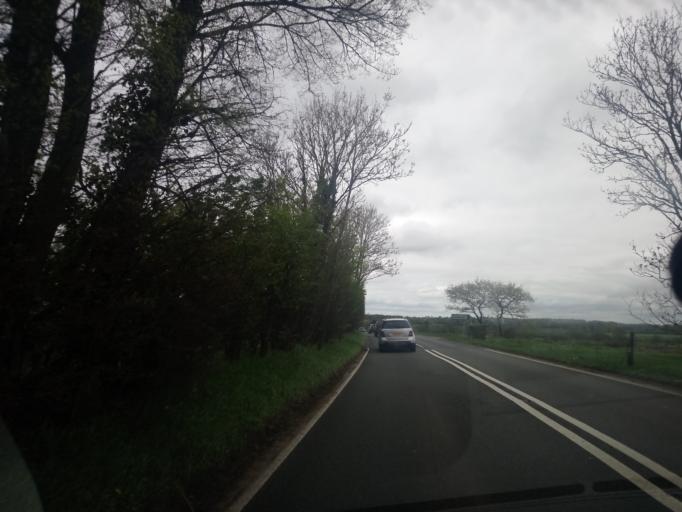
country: GB
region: England
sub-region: Telford and Wrekin
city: Chetwynd
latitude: 52.8213
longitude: -2.4517
